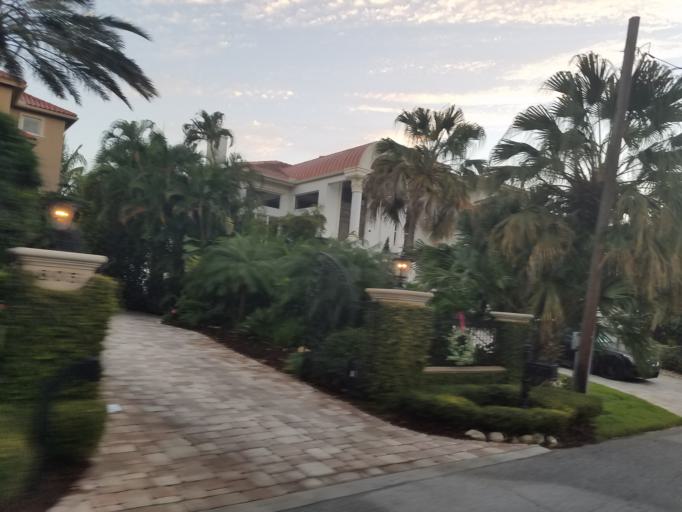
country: US
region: Florida
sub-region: Sarasota County
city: Siesta Key
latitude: 27.3033
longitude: -82.5499
